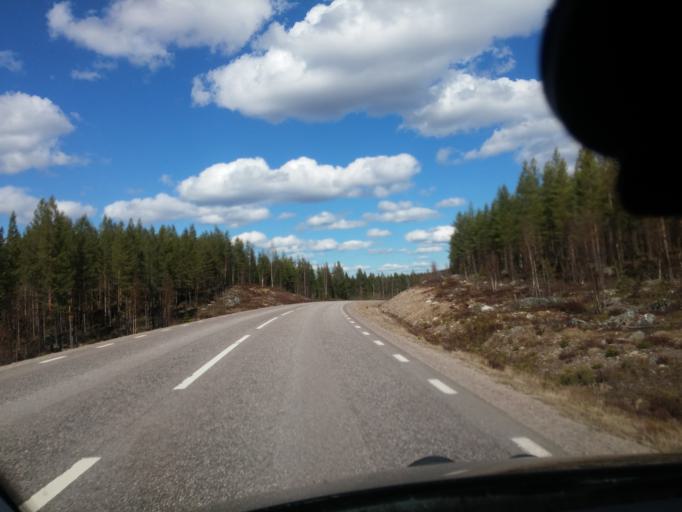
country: SE
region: Gaevleborg
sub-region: Ovanakers Kommun
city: Edsbyn
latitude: 61.2449
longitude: 15.8842
